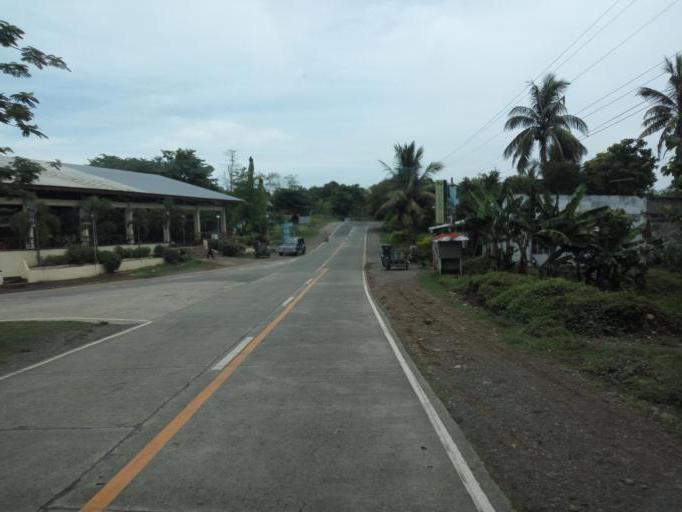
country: PH
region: Cagayan Valley
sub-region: Province of Quirino
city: Saguday
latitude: 16.5305
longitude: 121.5206
